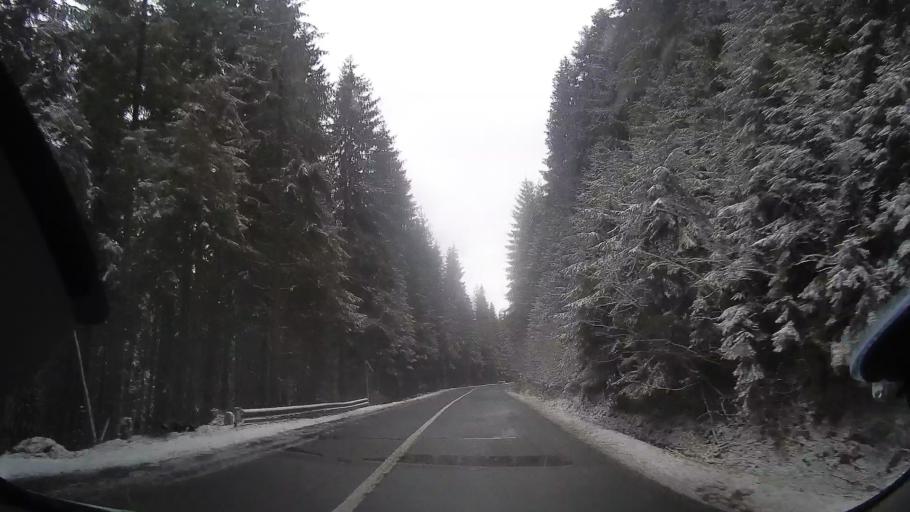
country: RO
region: Cluj
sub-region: Comuna Belis
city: Belis
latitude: 46.6544
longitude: 23.0524
